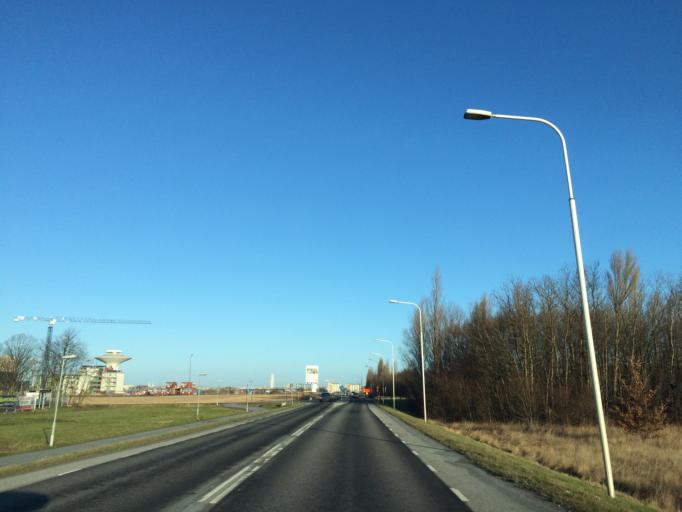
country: SE
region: Skane
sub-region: Malmo
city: Bunkeflostrand
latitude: 55.5570
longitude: 12.9836
